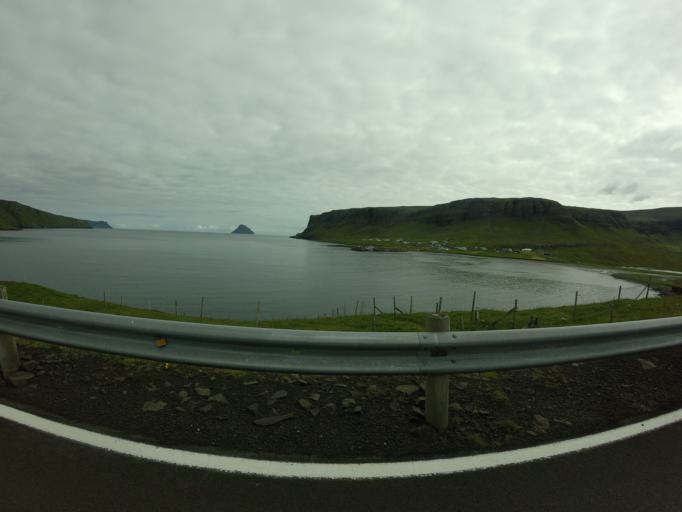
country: FO
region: Suduroy
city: Tvoroyri
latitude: 61.5951
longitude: -6.9447
